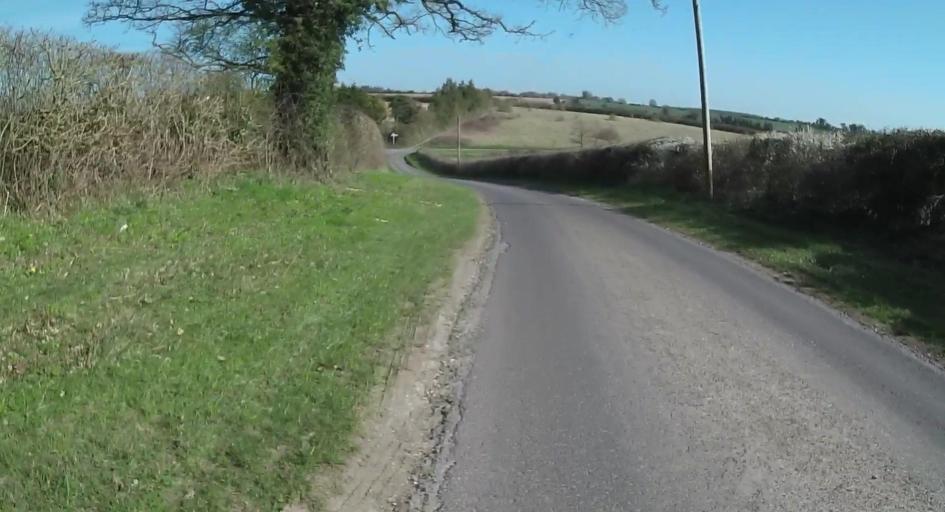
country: GB
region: England
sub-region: Hampshire
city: Highclere
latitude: 51.2601
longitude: -1.3848
